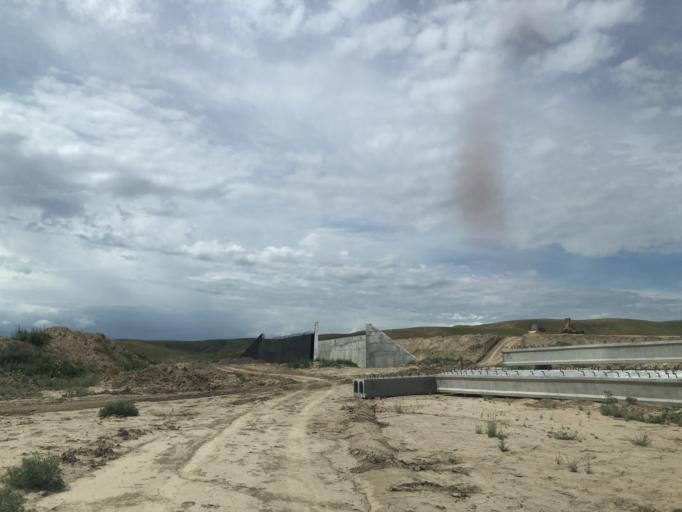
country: KZ
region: Almaty Oblysy
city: Burunday
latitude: 43.2966
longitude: 76.2241
